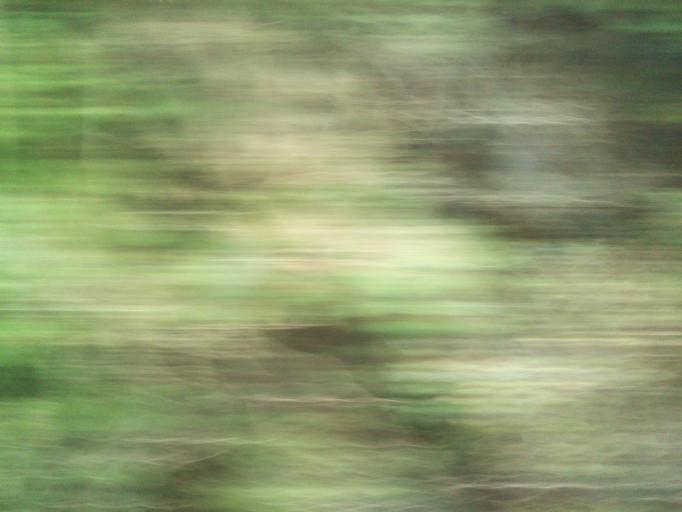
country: JP
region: Kochi
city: Nakamura
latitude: 32.9981
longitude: 132.9672
